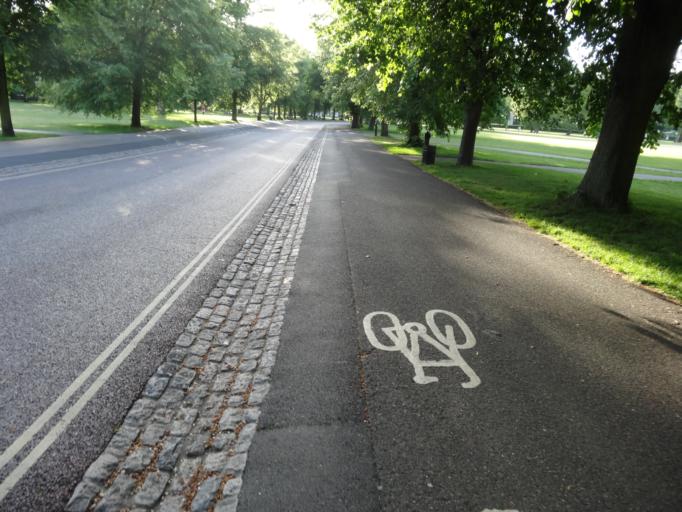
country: GB
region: England
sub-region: Greater London
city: Blackheath
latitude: 51.4782
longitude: -0.0044
